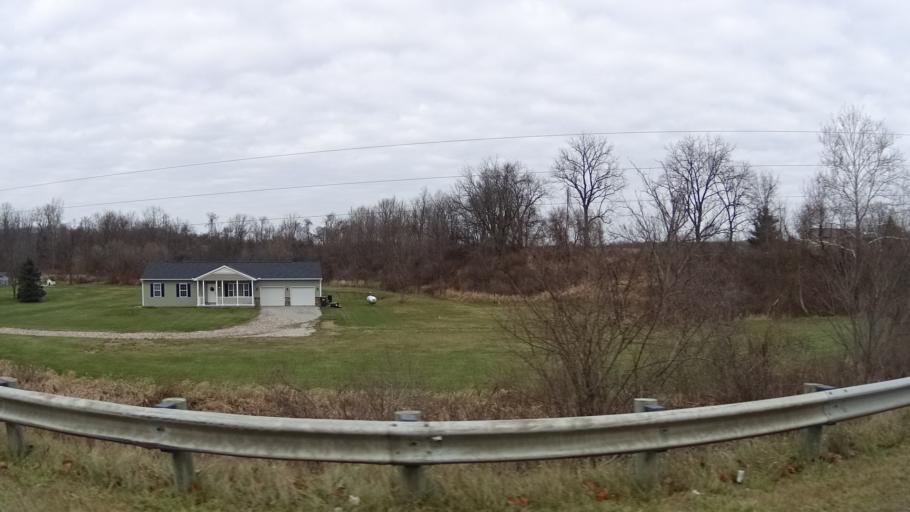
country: US
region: Ohio
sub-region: Lorain County
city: Camden
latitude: 41.1706
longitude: -82.2907
